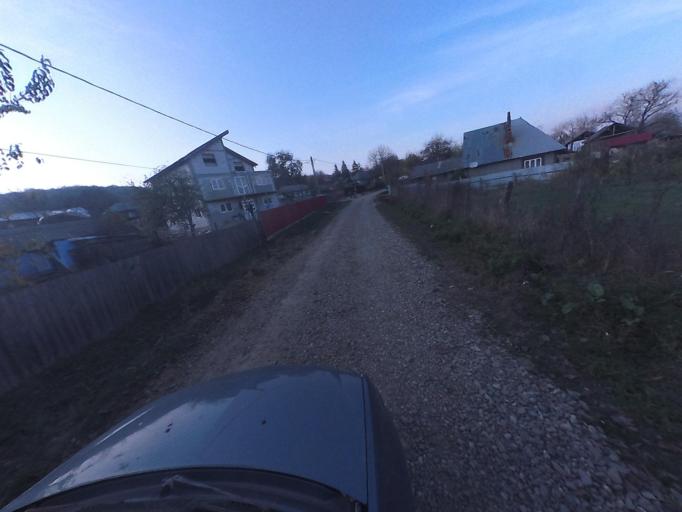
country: RO
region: Vaslui
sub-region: Comuna Bacesti
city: Bacesti
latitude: 46.7998
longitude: 27.2249
